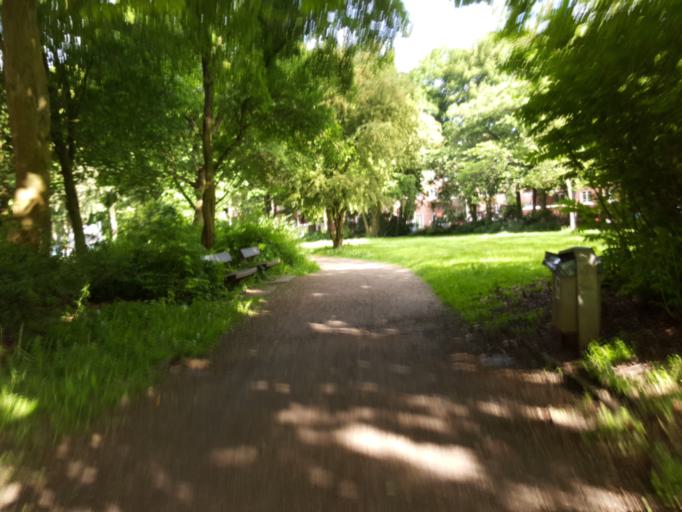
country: DE
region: Hamburg
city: Marienthal
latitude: 53.5573
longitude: 10.0644
